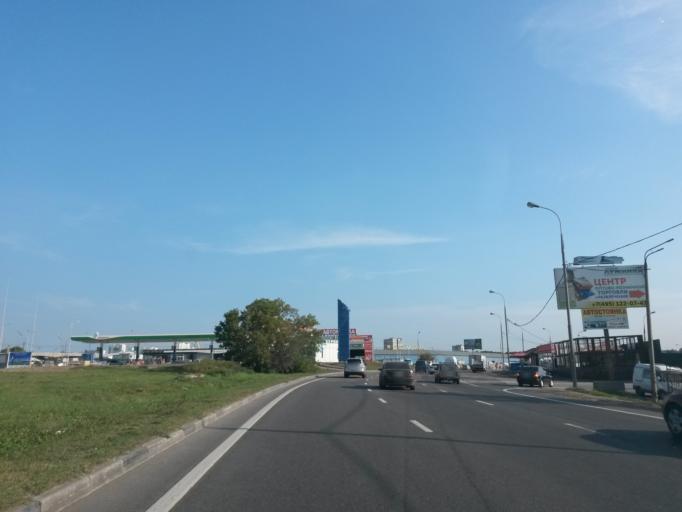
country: RU
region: Moscow
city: Annino
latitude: 55.5709
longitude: 37.6003
